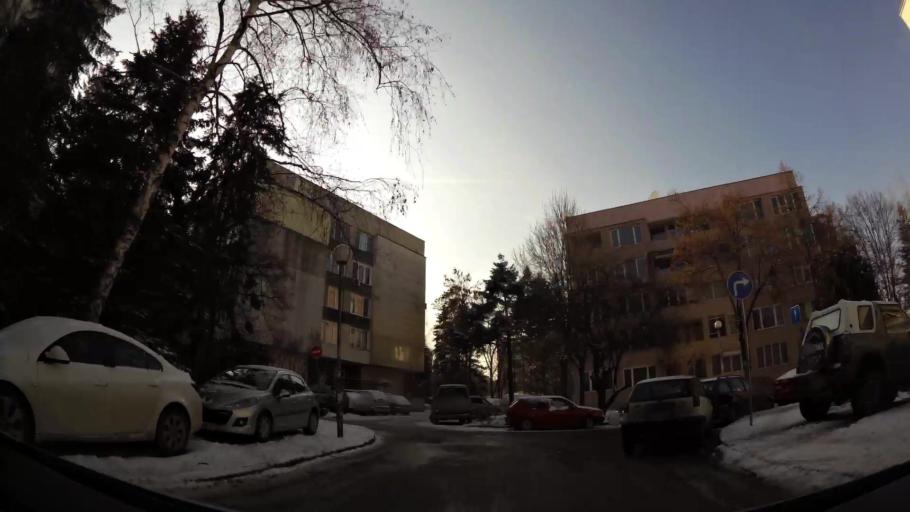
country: BG
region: Sofia-Capital
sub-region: Stolichna Obshtina
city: Sofia
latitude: 42.6630
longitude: 23.3471
